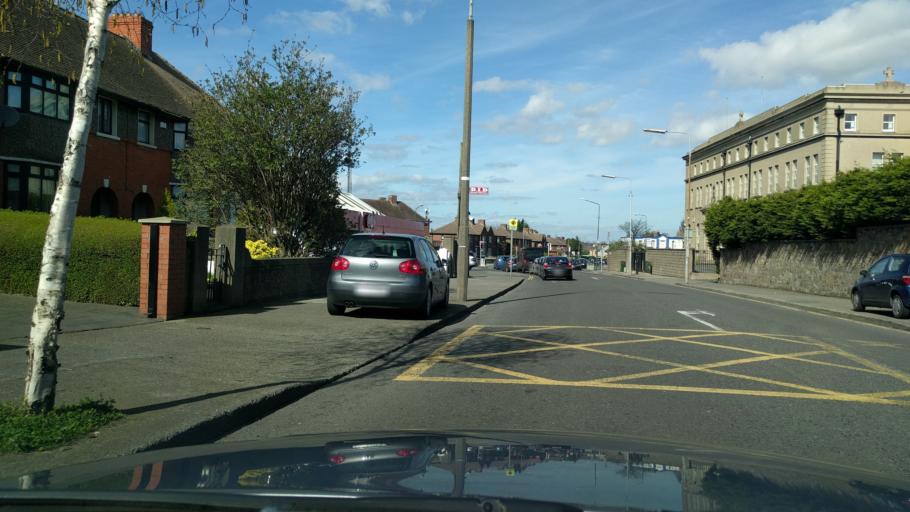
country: IE
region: Leinster
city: Rialto
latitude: 53.3291
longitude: -6.2982
